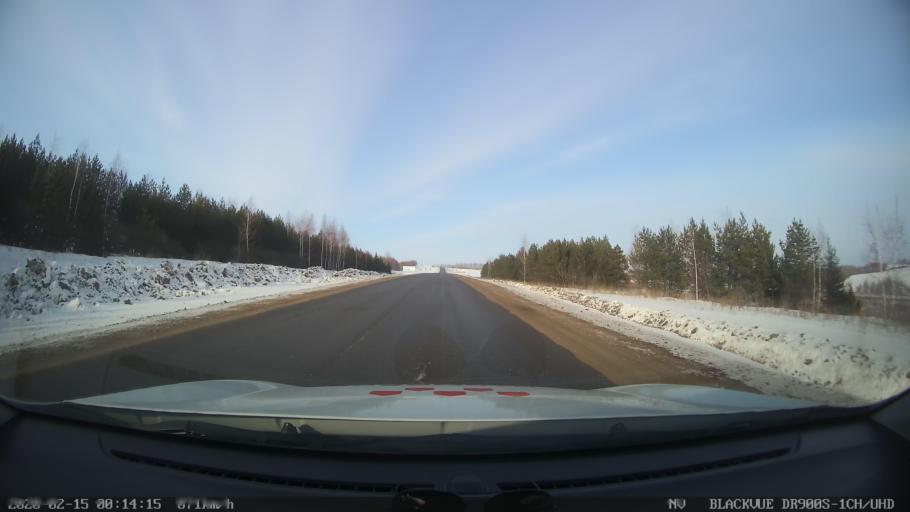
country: RU
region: Tatarstan
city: Stolbishchi
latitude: 55.4840
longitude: 49.0044
